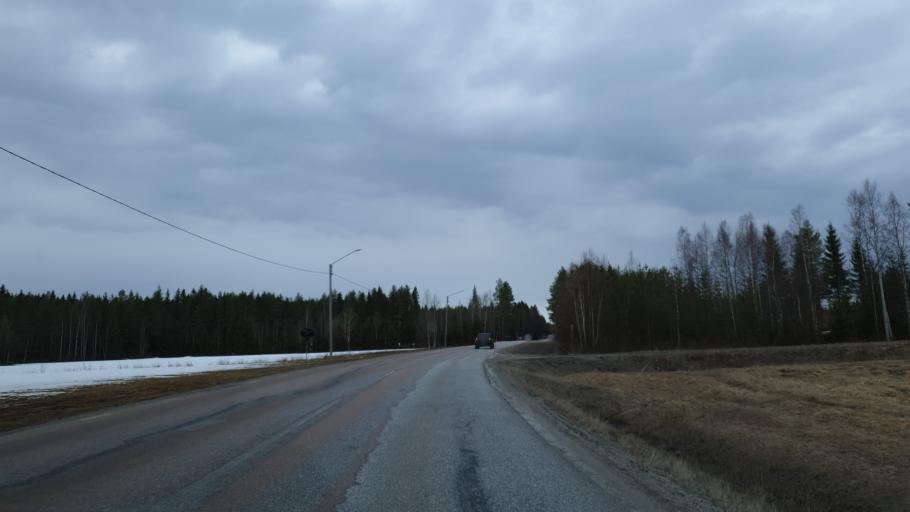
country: SE
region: Vaesterbotten
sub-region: Skelleftea Kommun
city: Viken
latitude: 64.6500
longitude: 20.9561
